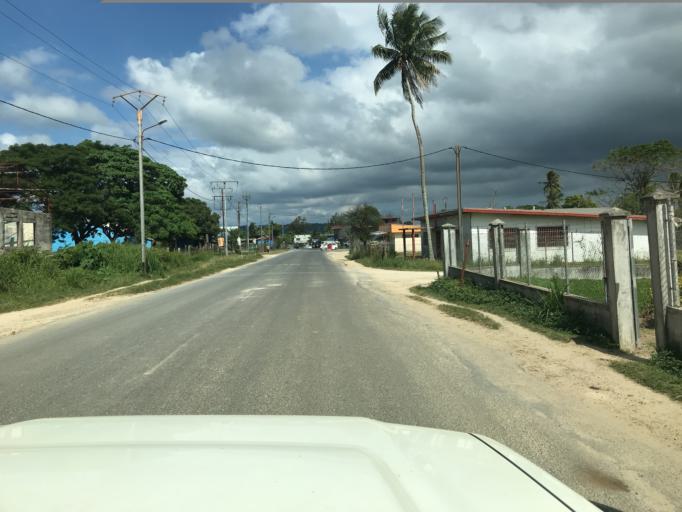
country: VU
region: Sanma
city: Luganville
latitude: -15.5112
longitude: 167.1775
